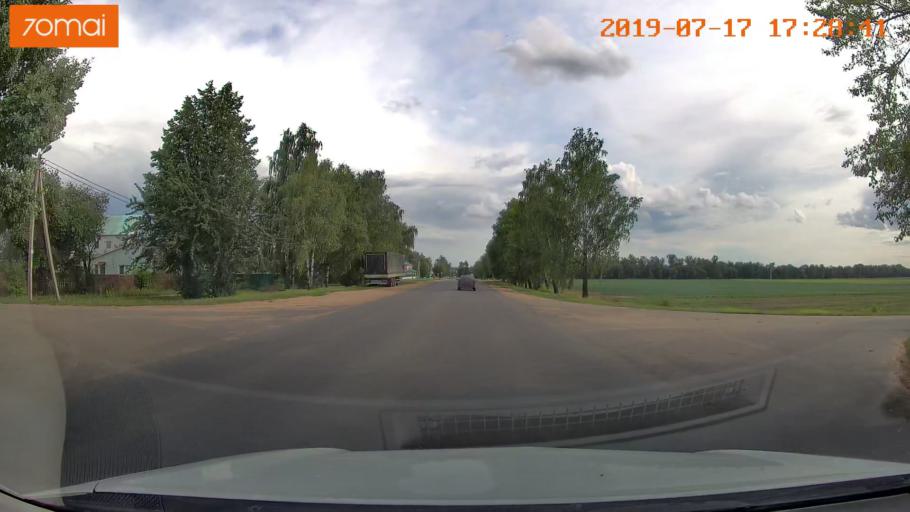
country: BY
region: Mogilev
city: Babruysk
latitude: 53.1278
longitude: 29.1666
